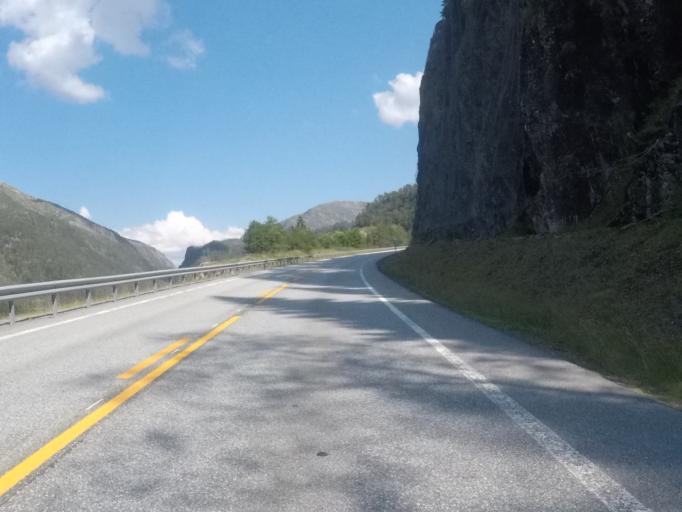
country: NO
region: Hordaland
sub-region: Modalen
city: Mo
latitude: 60.7749
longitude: 5.6230
